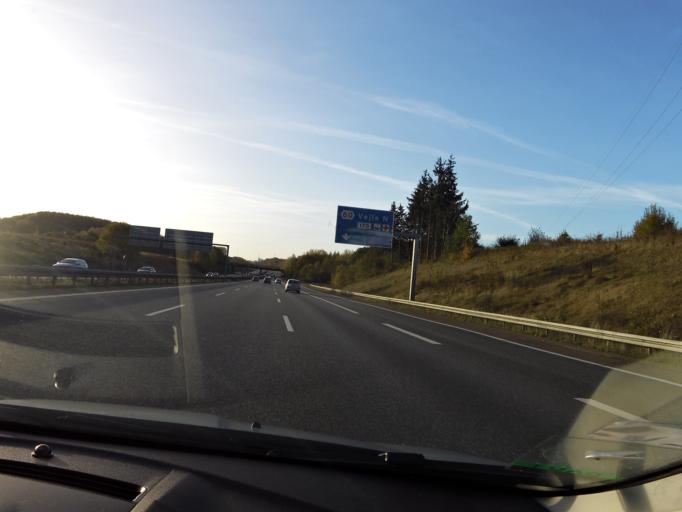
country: DK
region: South Denmark
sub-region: Vejle Kommune
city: Vejle
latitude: 55.7280
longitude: 9.5760
